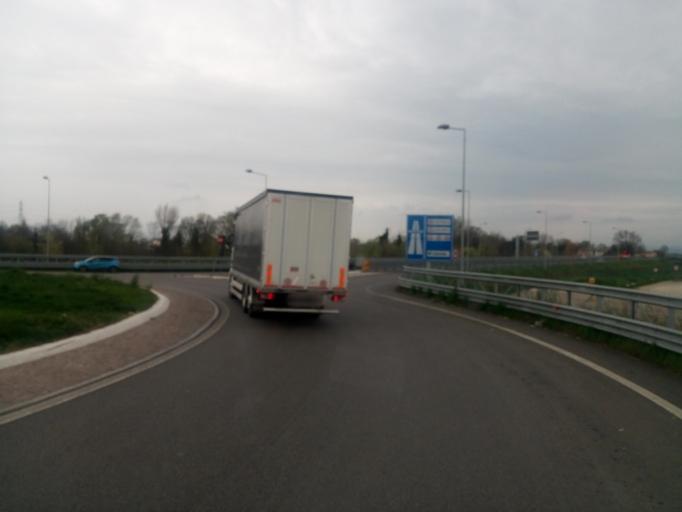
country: IT
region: Emilia-Romagna
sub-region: Forli-Cesena
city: Forli
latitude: 44.2470
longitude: 12.0944
